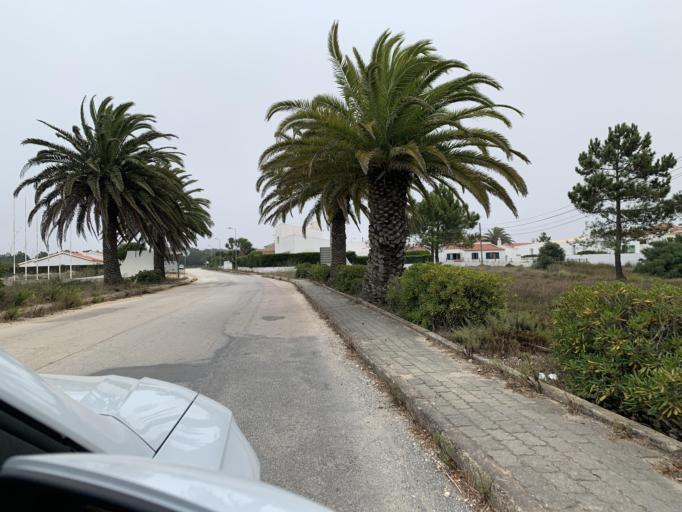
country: PT
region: Faro
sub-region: Aljezur
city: Aljezur
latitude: 37.3027
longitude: -8.8490
